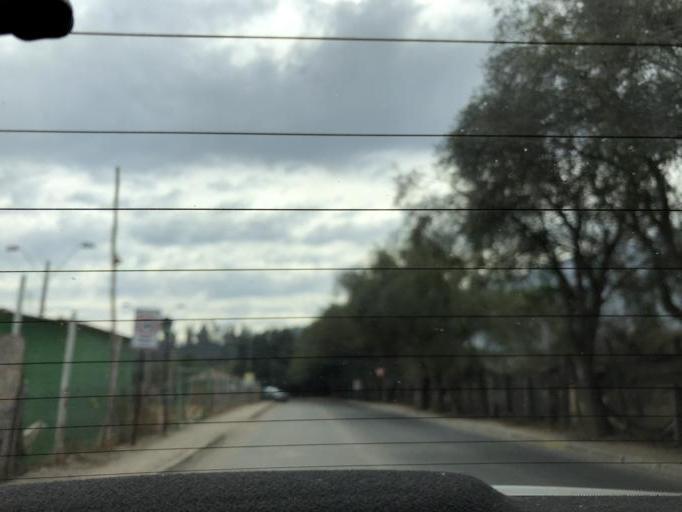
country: CL
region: Santiago Metropolitan
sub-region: Provincia de Cordillera
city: Puente Alto
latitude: -33.5965
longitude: -70.5149
